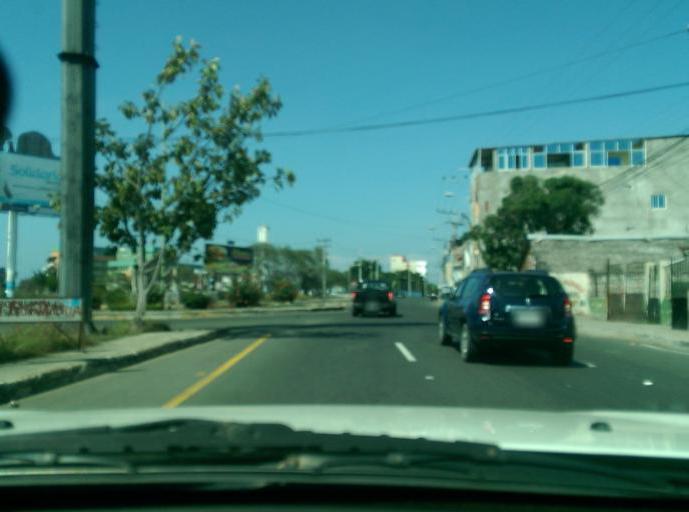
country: EC
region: Manabi
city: Manta
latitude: -0.9558
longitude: -80.7447
